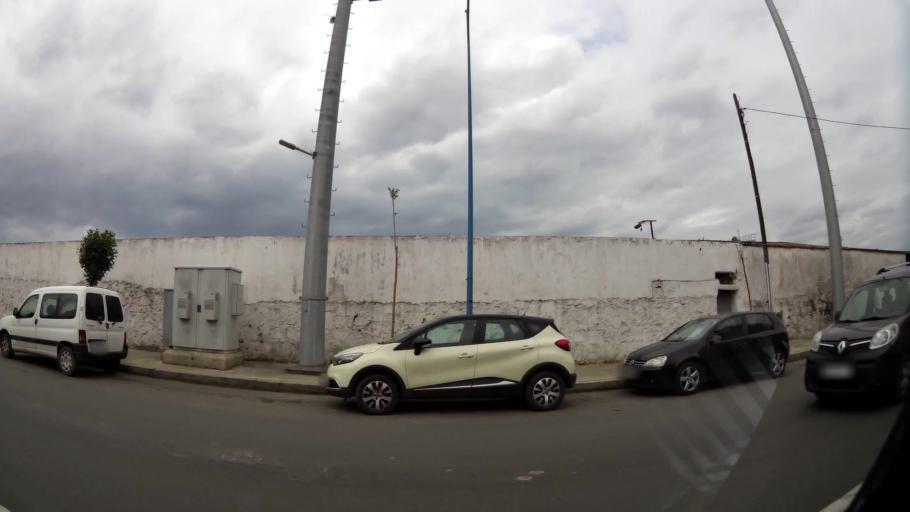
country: MA
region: Grand Casablanca
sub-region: Casablanca
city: Casablanca
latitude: 33.5958
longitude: -7.5637
